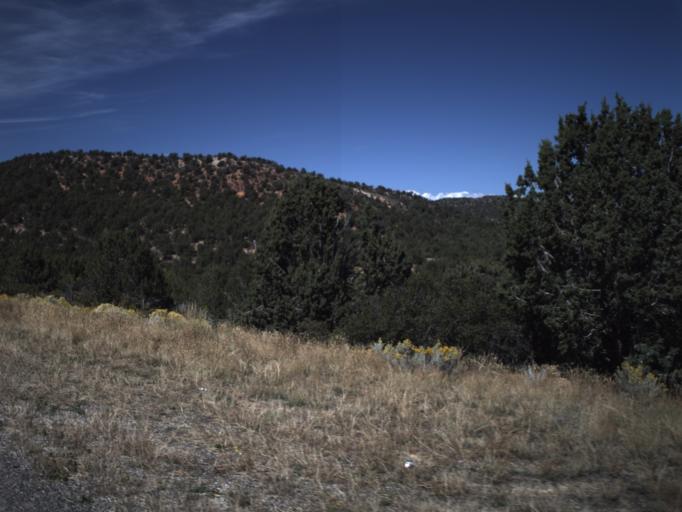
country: US
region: Utah
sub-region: Washington County
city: Enterprise
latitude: 37.5240
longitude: -113.6412
